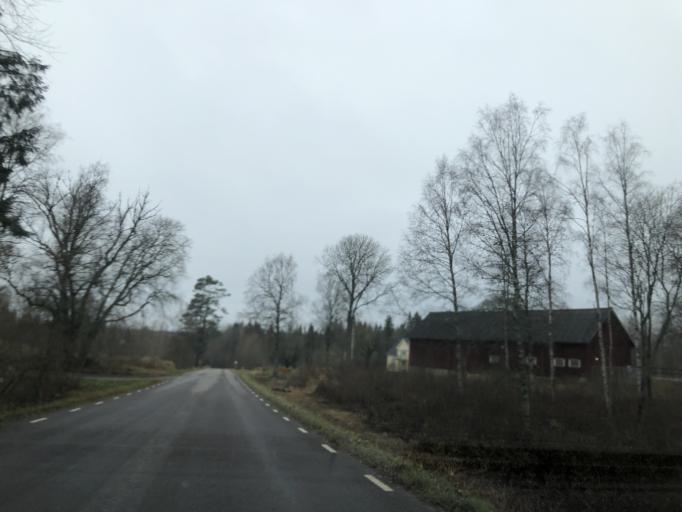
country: SE
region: Vaestra Goetaland
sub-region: Ulricehamns Kommun
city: Ulricehamn
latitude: 57.7657
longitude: 13.4679
